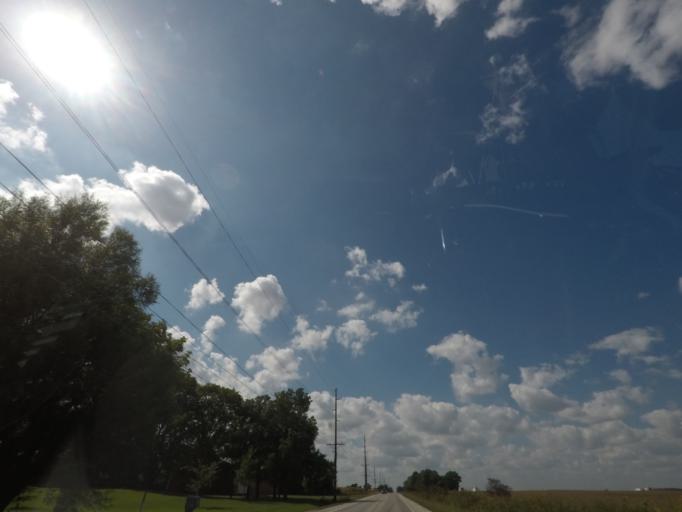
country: US
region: Iowa
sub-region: Story County
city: Nevada
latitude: 42.0231
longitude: -93.5291
